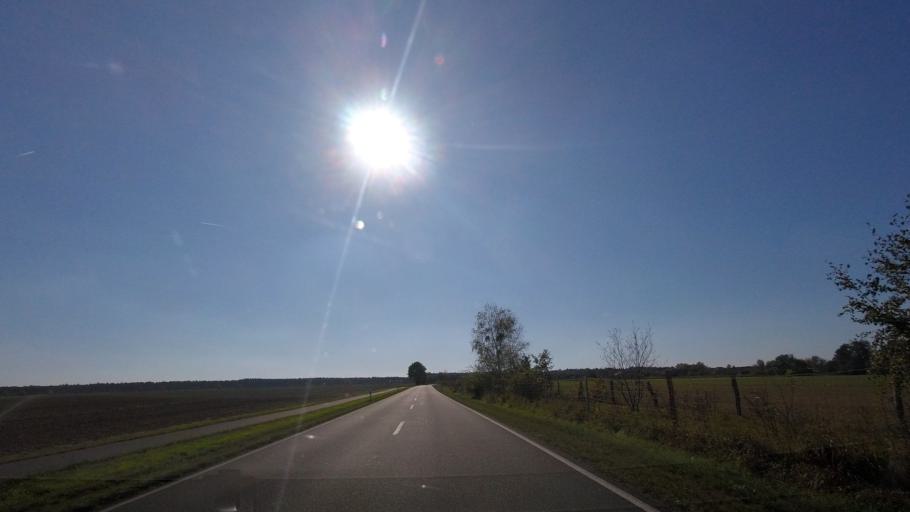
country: DE
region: Saxony-Anhalt
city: Muhlanger
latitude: 51.8628
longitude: 12.7812
